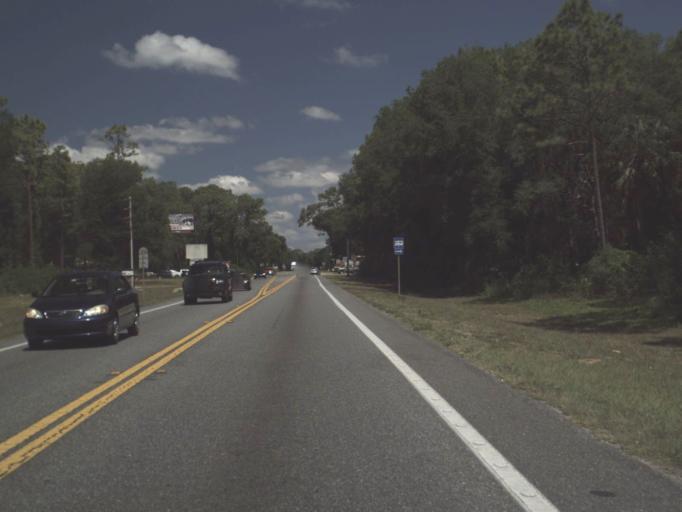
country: US
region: Florida
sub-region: Marion County
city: Silver Springs Shores
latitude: 29.1933
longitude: -81.9113
